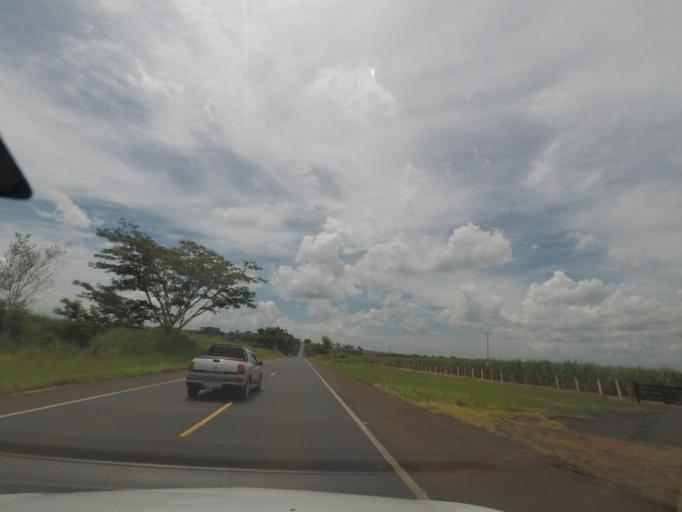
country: BR
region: Sao Paulo
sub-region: Barretos
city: Barretos
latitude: -20.4086
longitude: -48.6343
